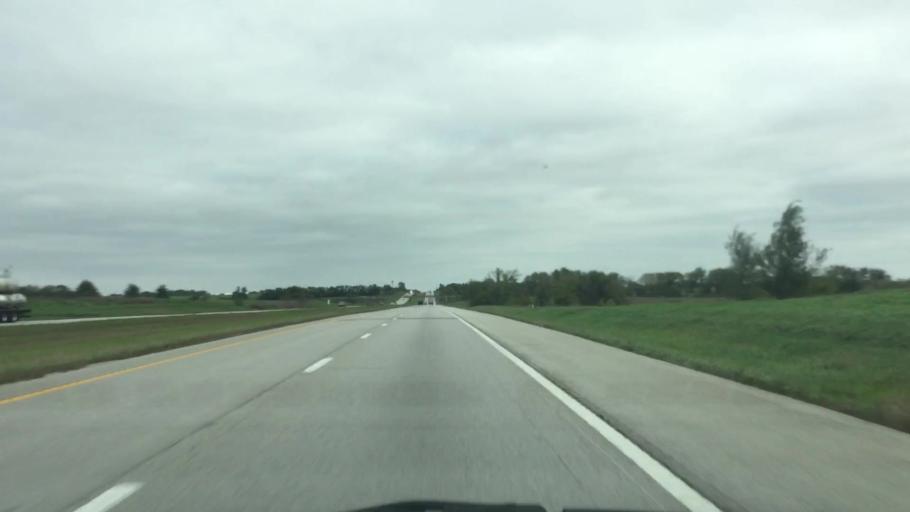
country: US
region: Missouri
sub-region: Clinton County
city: Cameron
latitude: 39.7975
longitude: -94.2015
